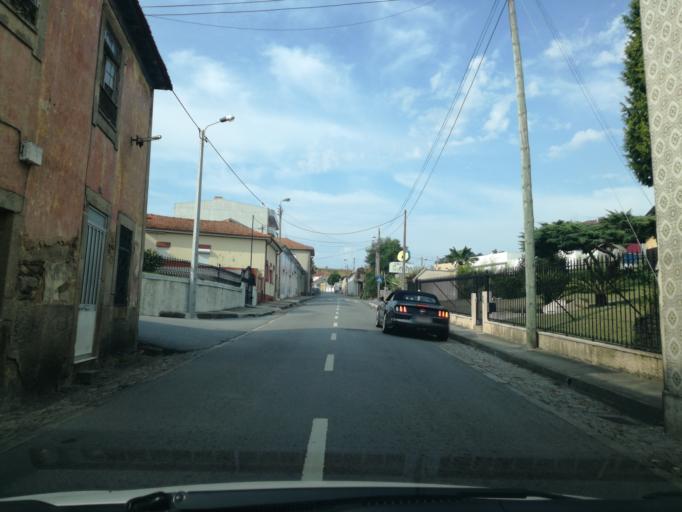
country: PT
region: Porto
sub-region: Vila Nova de Gaia
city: Sao Felix da Marinha
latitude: 41.0406
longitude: -8.6293
